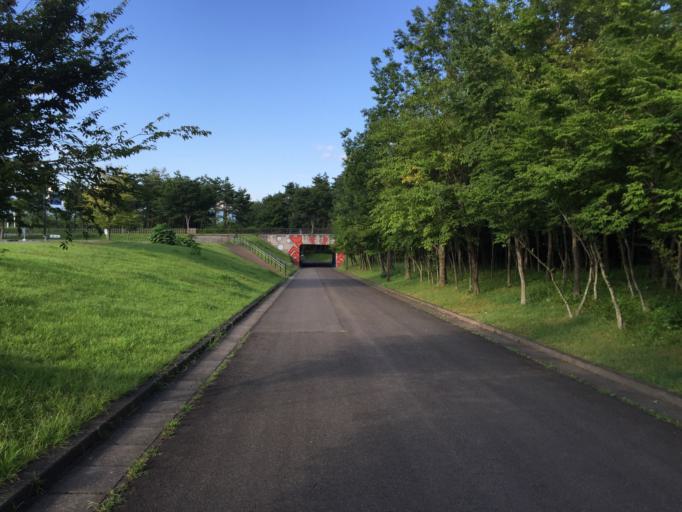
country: JP
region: Fukushima
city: Fukushima-shi
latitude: 37.7181
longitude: 140.3599
